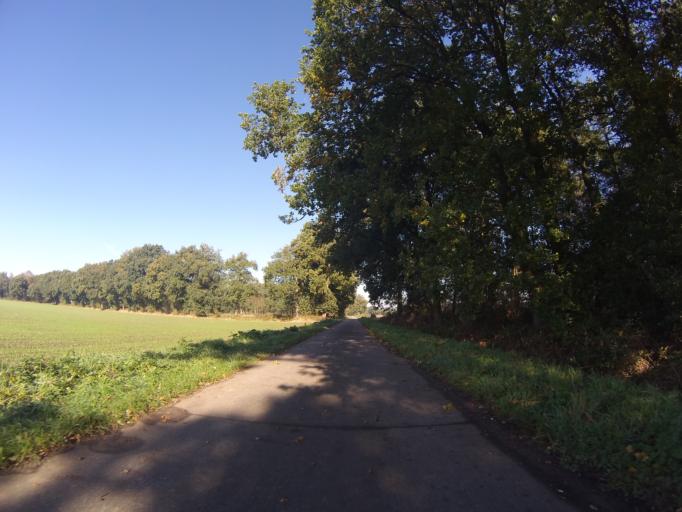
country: NL
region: Drenthe
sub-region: Gemeente Coevorden
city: Dalen
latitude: 52.7334
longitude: 6.6783
